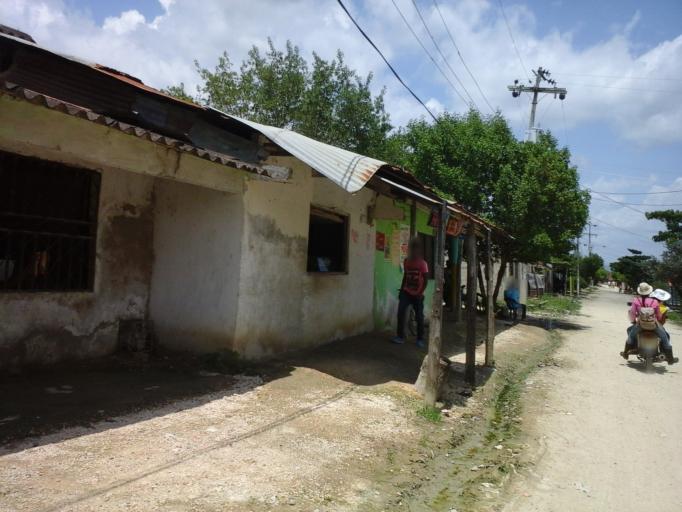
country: CO
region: Bolivar
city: San Pablo
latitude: 10.1441
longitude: -75.2767
